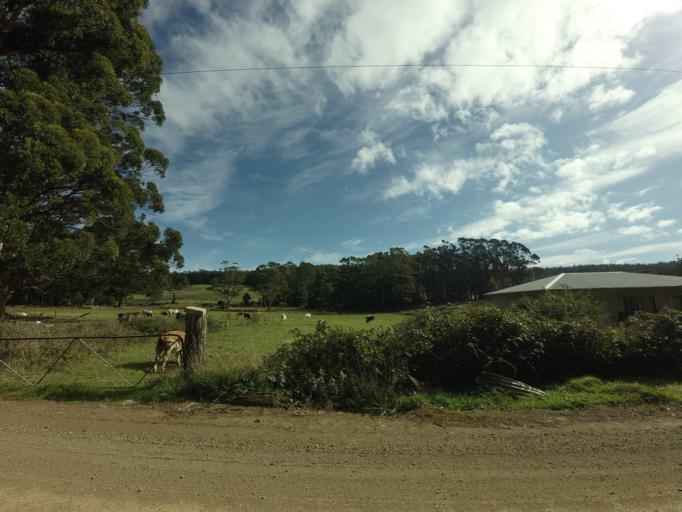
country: AU
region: Tasmania
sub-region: Clarence
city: Sandford
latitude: -43.1514
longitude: 147.7635
